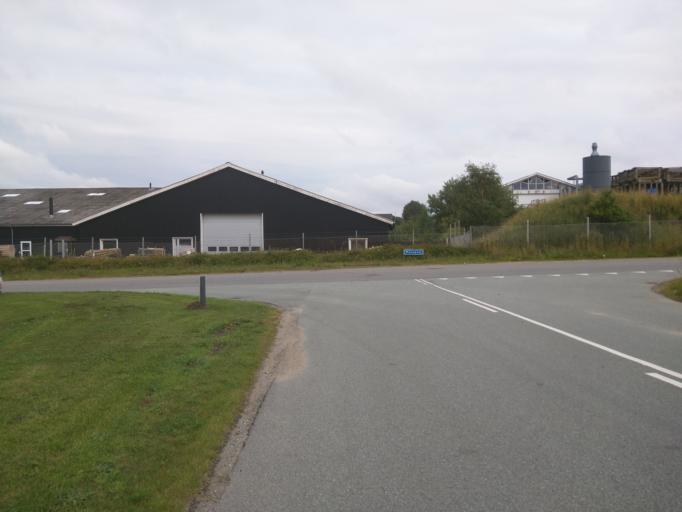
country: DK
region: Central Jutland
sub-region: Viborg Kommune
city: Viborg
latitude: 56.4520
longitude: 9.3644
